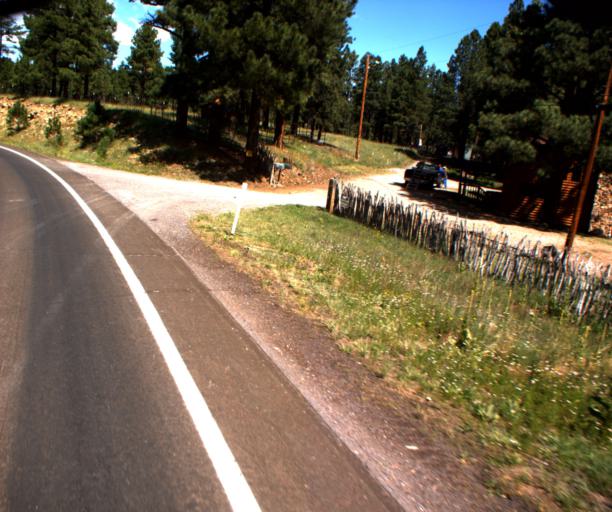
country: US
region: Arizona
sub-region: Apache County
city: Eagar
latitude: 34.0598
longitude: -109.4621
